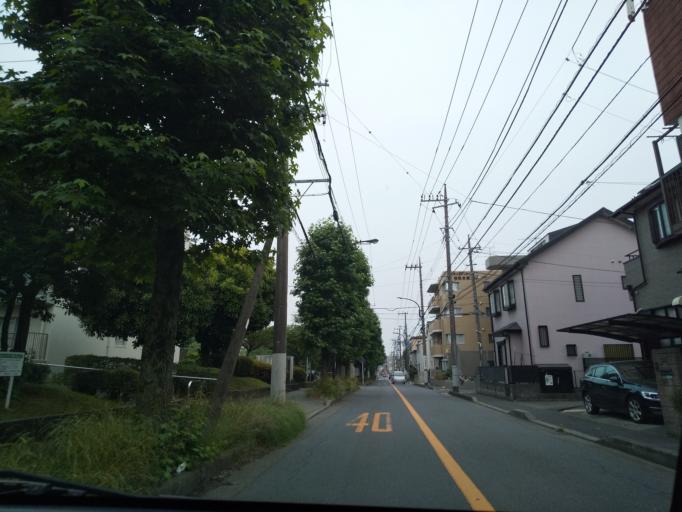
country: JP
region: Kanagawa
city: Zama
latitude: 35.5075
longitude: 139.4030
